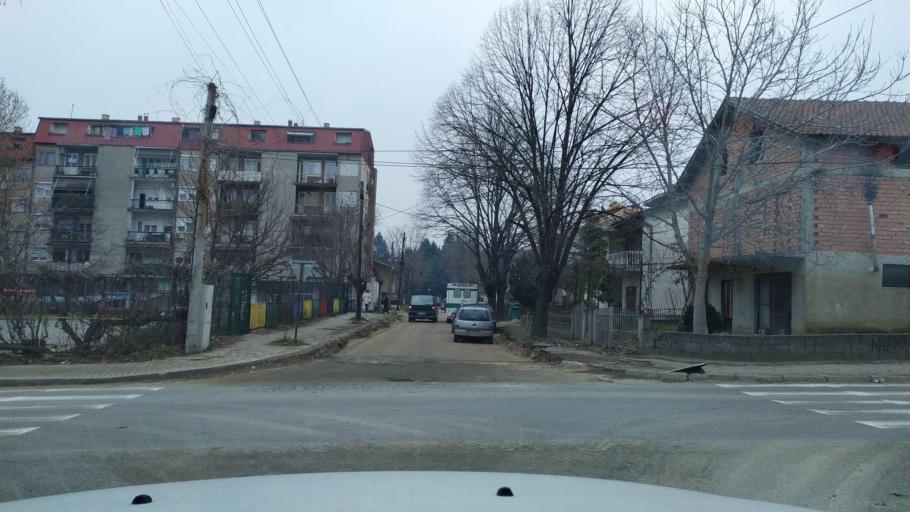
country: MK
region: Negotino
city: Negotino
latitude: 41.4816
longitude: 22.0819
